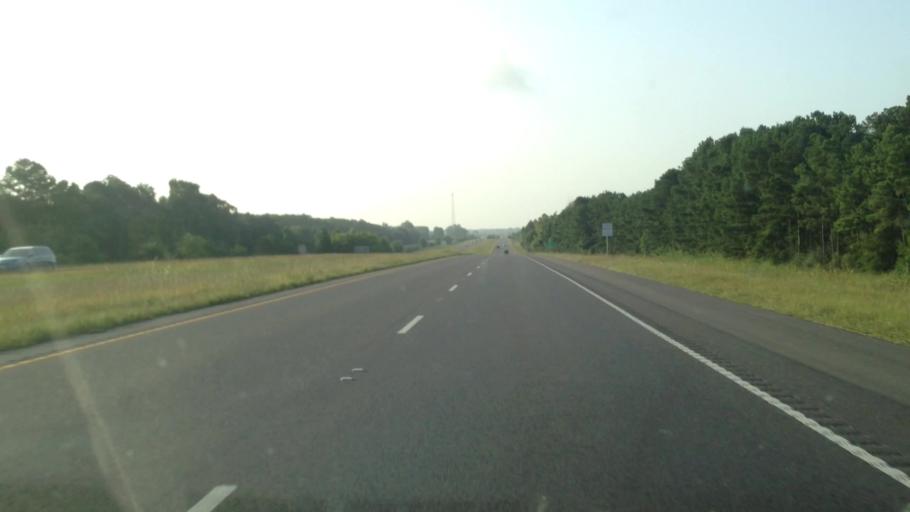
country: US
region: Louisiana
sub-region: Rapides Parish
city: Boyce
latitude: 31.4019
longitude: -92.7064
